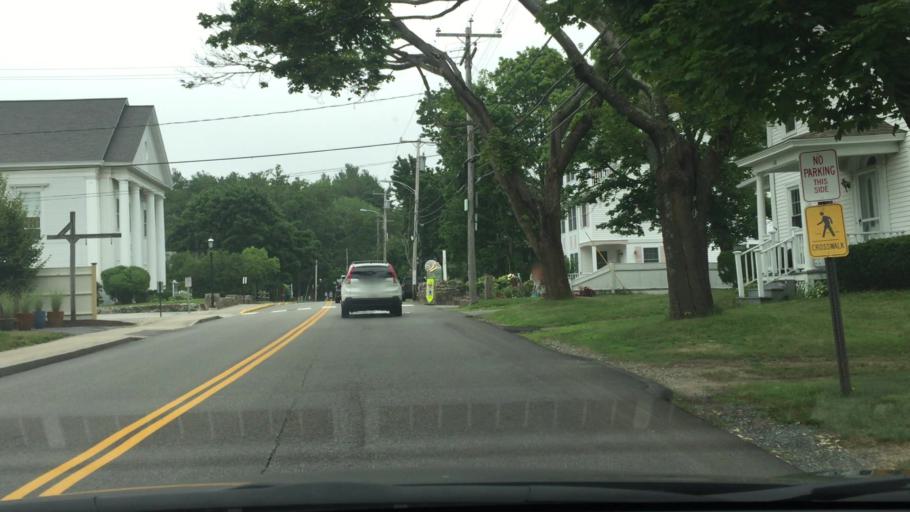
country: US
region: Maine
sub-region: York County
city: Ogunquit
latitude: 43.2447
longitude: -70.5968
